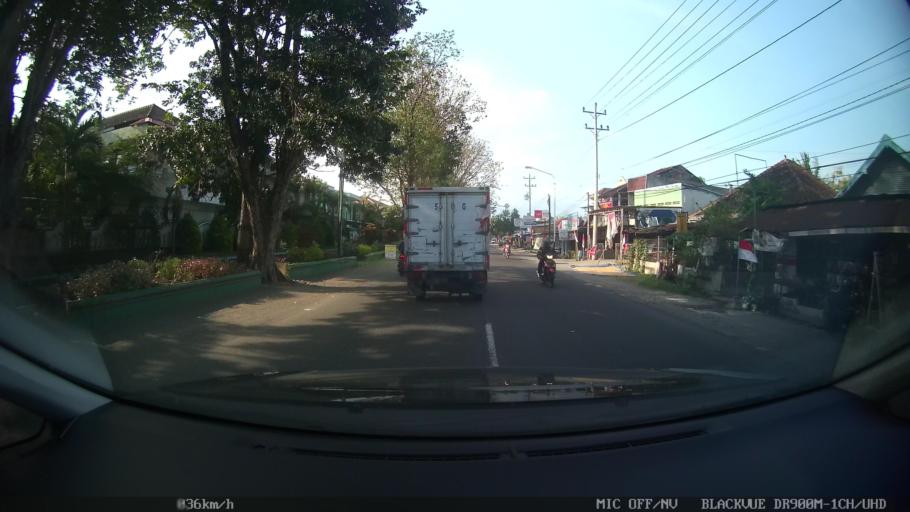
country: ID
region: Daerah Istimewa Yogyakarta
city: Bantul
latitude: -7.8993
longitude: 110.3223
